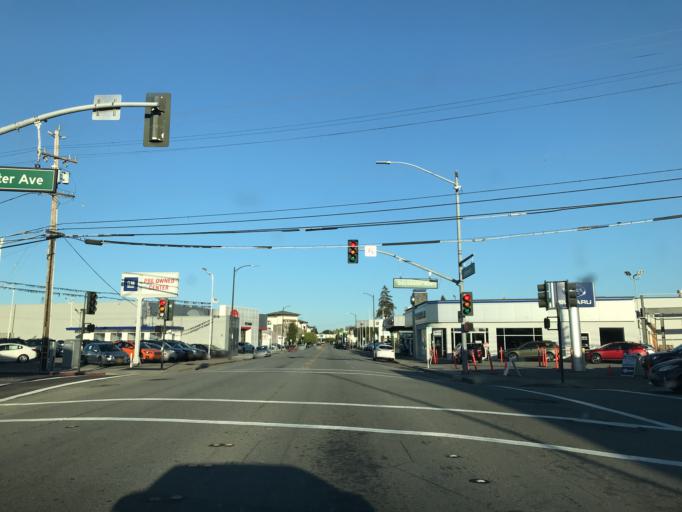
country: US
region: California
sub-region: San Mateo County
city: San Mateo
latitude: 37.5780
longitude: -122.3417
